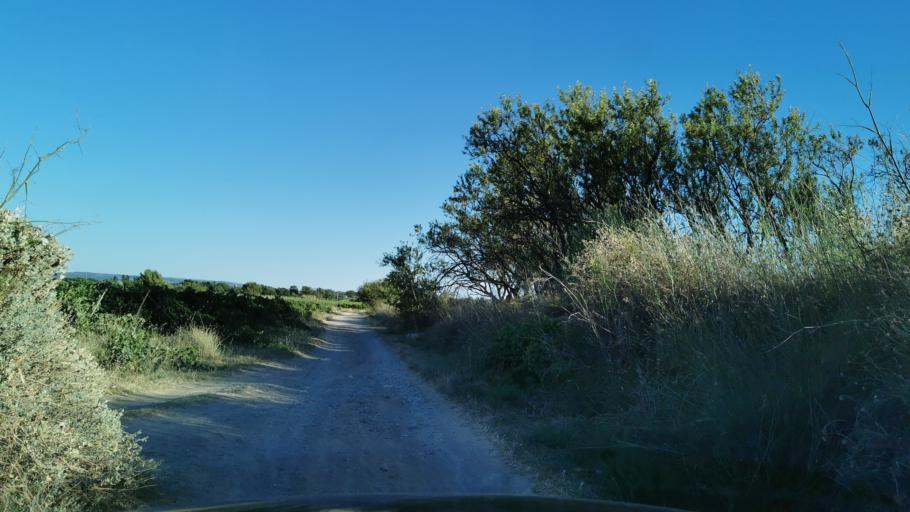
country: FR
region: Languedoc-Roussillon
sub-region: Departement de l'Aude
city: Ouveillan
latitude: 43.2670
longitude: 2.9819
